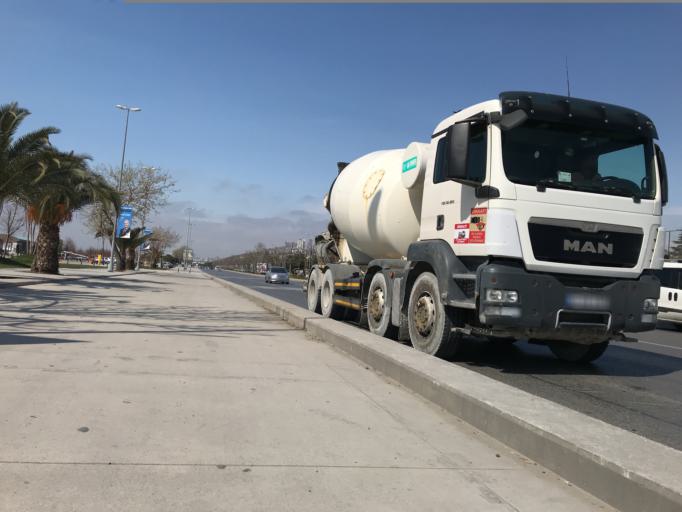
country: TR
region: Istanbul
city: Maltepe
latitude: 40.9230
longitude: 29.1256
